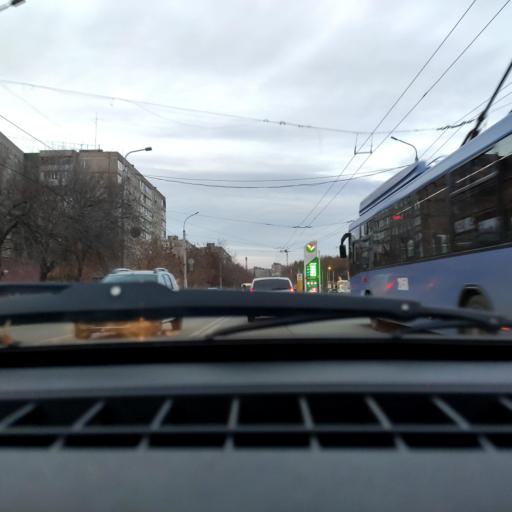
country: RU
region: Bashkortostan
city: Ufa
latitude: 54.6975
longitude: 56.0067
